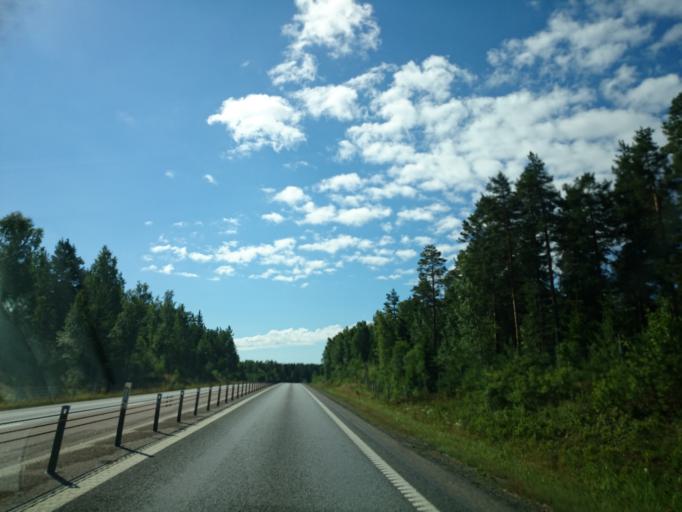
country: SE
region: Gaevleborg
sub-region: Soderhamns Kommun
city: Soderhamn
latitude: 61.2625
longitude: 17.0321
